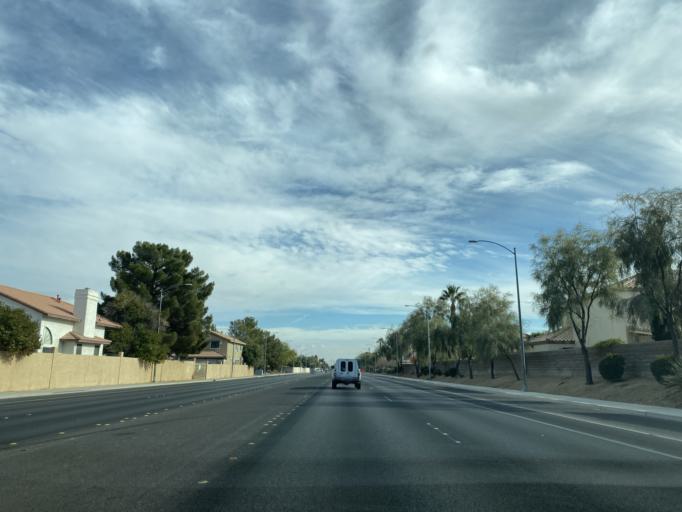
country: US
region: Nevada
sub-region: Clark County
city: Las Vegas
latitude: 36.2465
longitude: -115.2152
